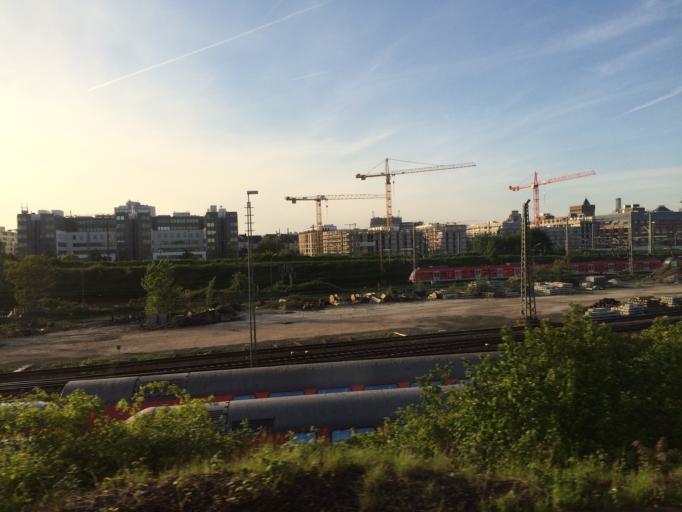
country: DE
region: Hesse
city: Niederrad
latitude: 50.0967
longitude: 8.6391
